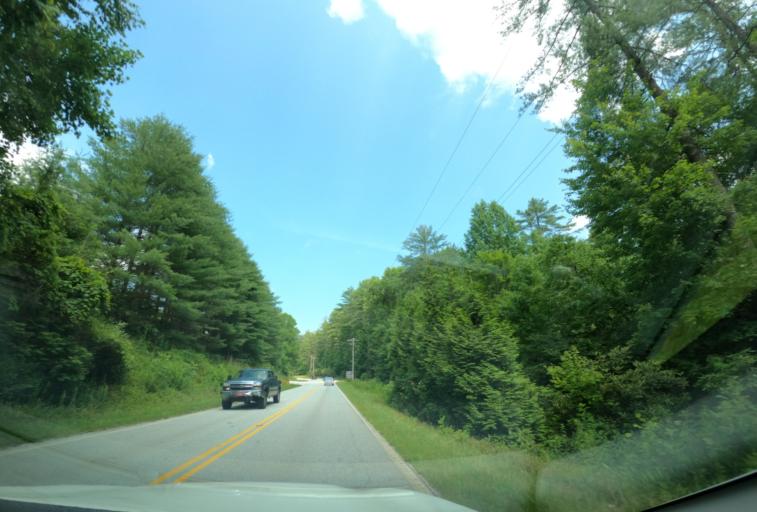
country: US
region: North Carolina
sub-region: Transylvania County
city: Brevard
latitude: 35.0925
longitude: -82.9739
